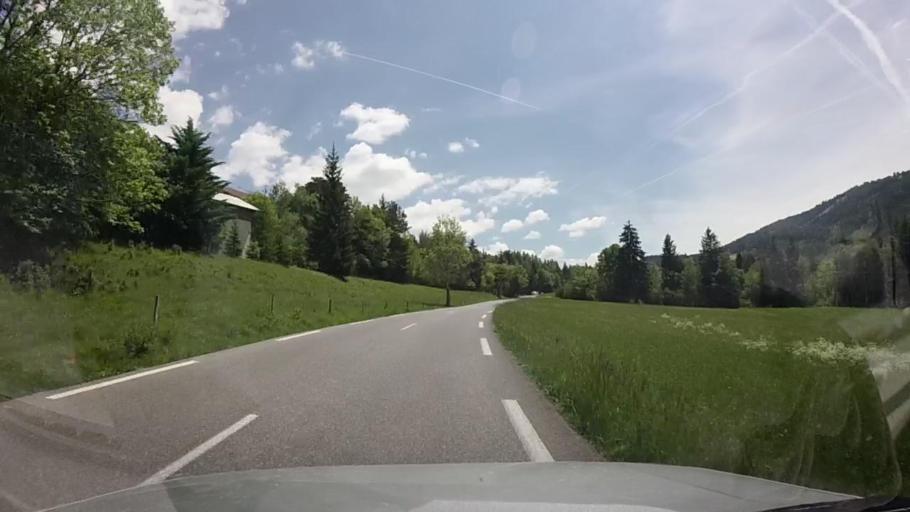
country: FR
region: Provence-Alpes-Cote d'Azur
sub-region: Departement des Alpes-de-Haute-Provence
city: Seyne-les-Alpes
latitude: 44.3334
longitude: 6.3896
